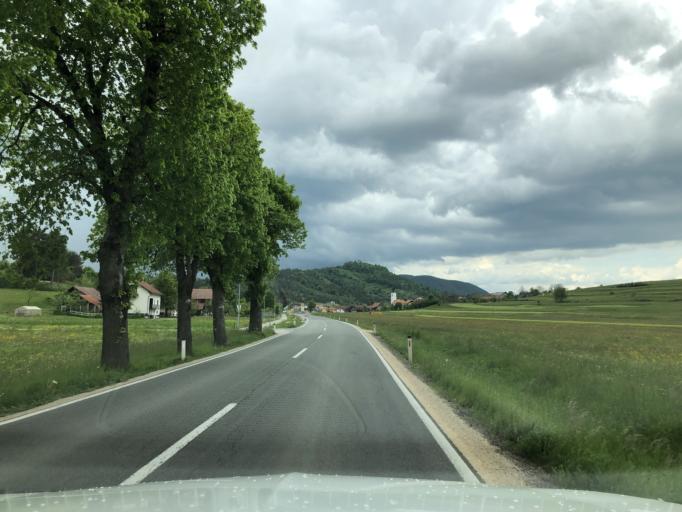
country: SI
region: Cerknica
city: Rakek
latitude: 45.8170
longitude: 14.2985
